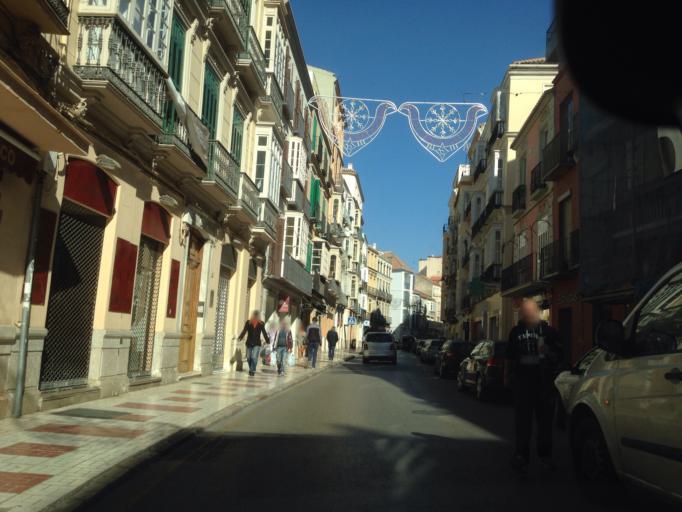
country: ES
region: Andalusia
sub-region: Provincia de Malaga
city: Malaga
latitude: 36.7227
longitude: -4.4243
